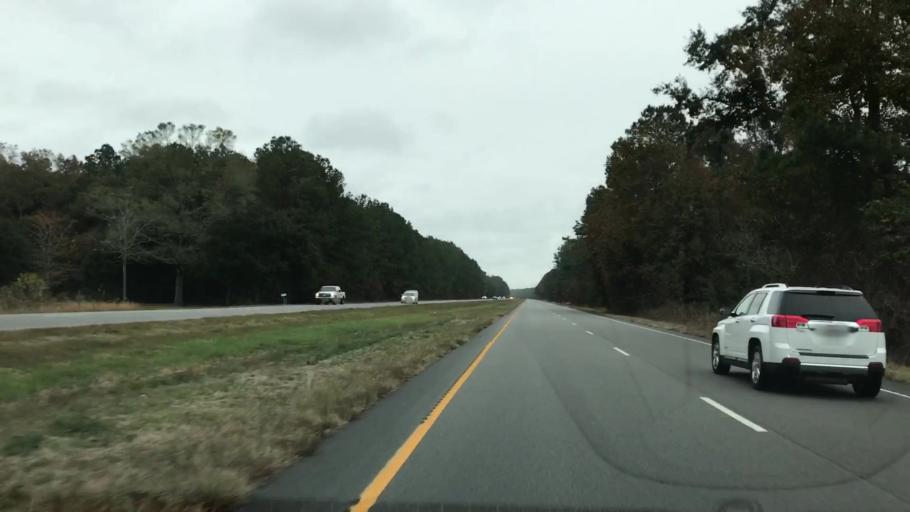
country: US
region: South Carolina
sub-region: Charleston County
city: Awendaw
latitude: 33.1114
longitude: -79.4598
